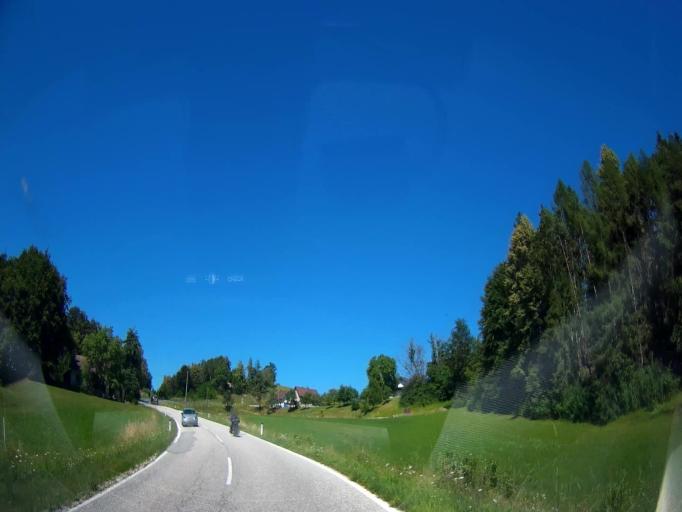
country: AT
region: Carinthia
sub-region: Politischer Bezirk Klagenfurt Land
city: Grafenstein
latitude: 46.5418
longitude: 14.4145
